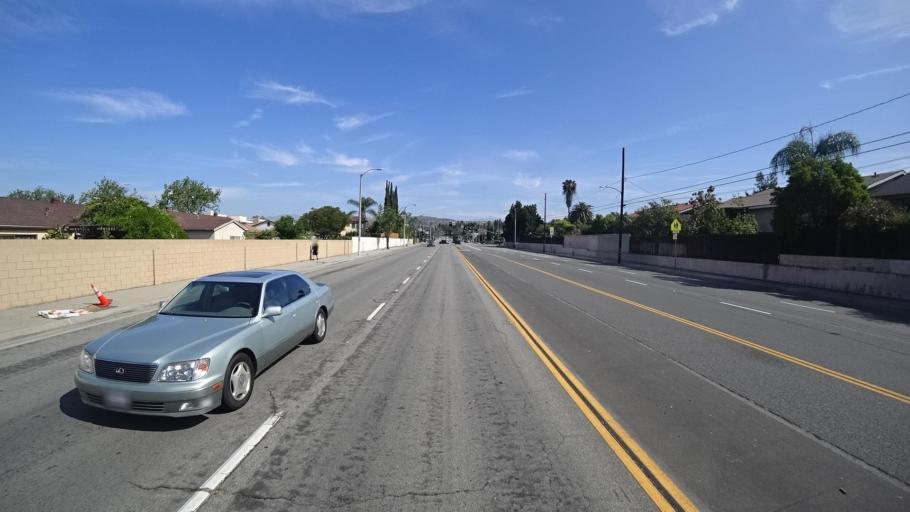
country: US
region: California
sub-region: Los Angeles County
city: South San Jose Hills
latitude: 34.0071
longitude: -117.8873
